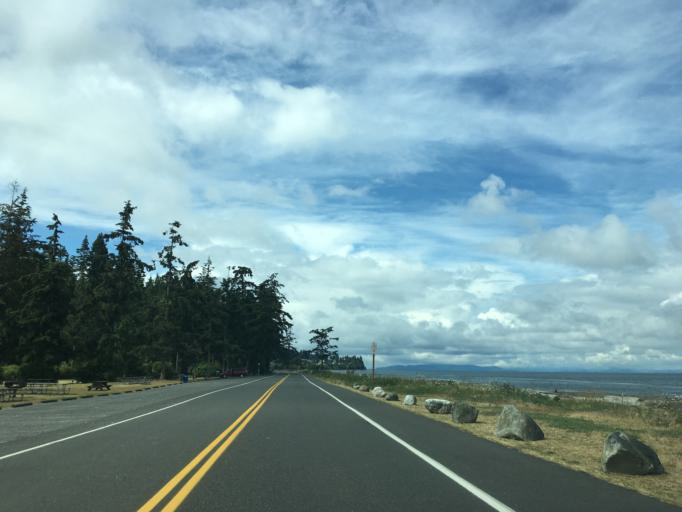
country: US
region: Washington
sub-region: Whatcom County
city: Birch Bay
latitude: 48.9062
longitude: -122.7667
